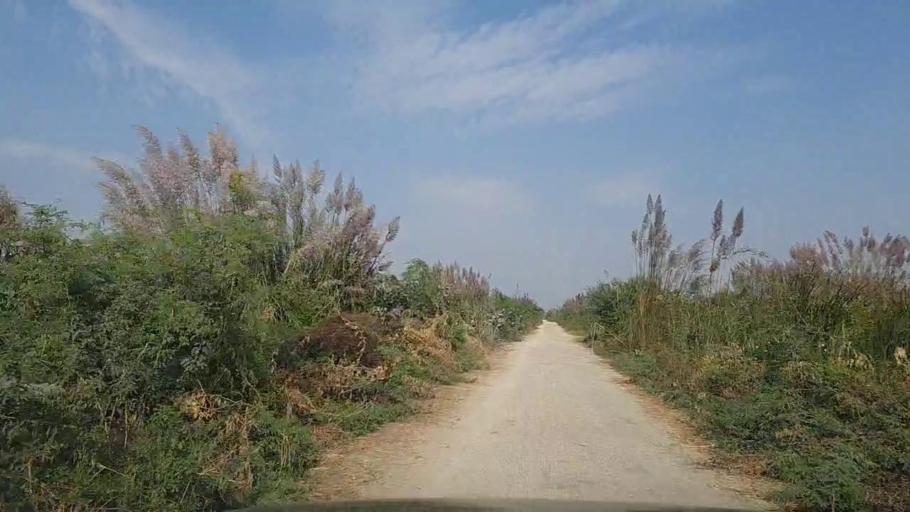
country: PK
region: Sindh
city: Thatta
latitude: 24.7644
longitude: 67.7690
